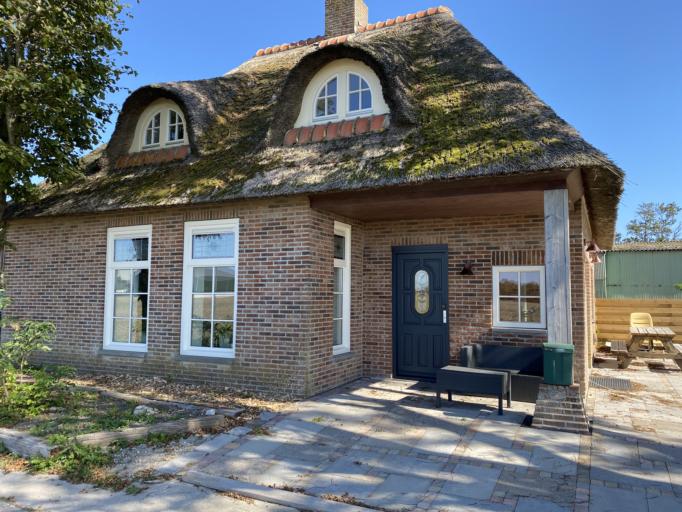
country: NL
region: Friesland
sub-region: Gemeente Het Bildt
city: Sint Jacobiparochie
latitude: 53.2879
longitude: 5.6162
